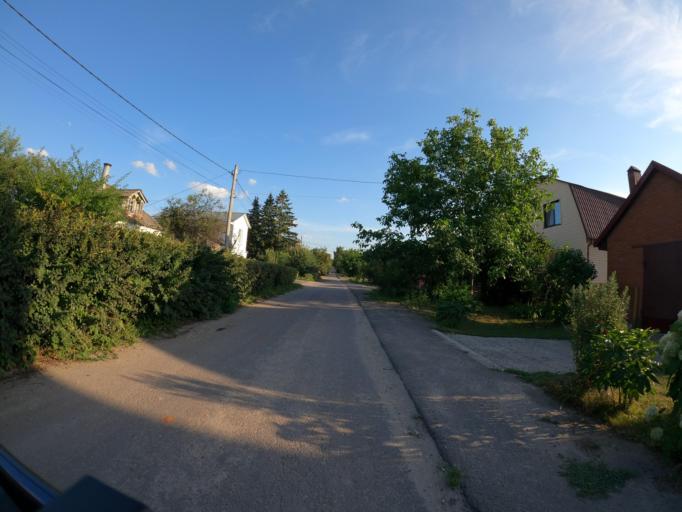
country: RU
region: Moskovskaya
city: Raduzhnyy
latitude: 55.1123
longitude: 38.7325
